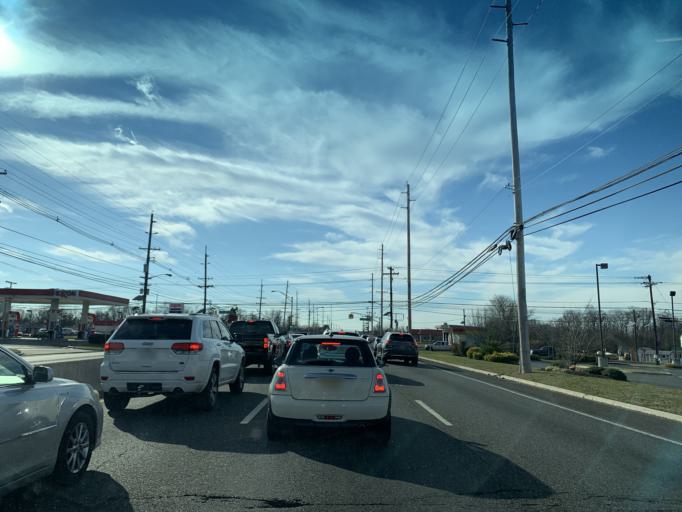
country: US
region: New Jersey
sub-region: Burlington County
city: Beverly
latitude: 40.0393
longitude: -74.9148
